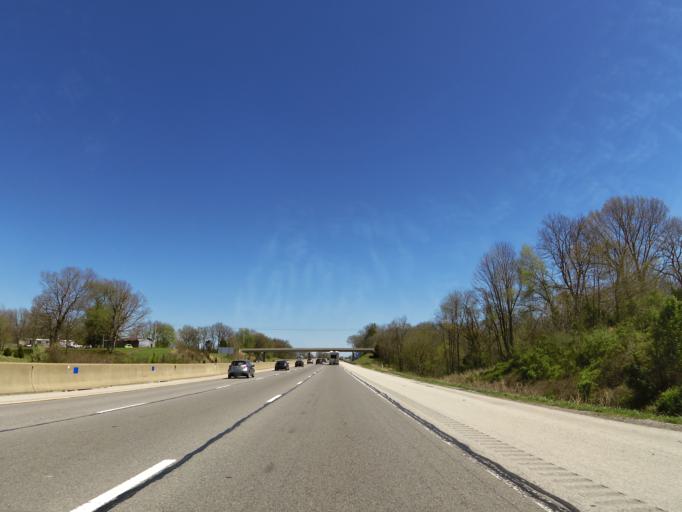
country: US
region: Kentucky
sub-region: Warren County
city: Bowling Green
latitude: 37.0091
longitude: -86.3546
